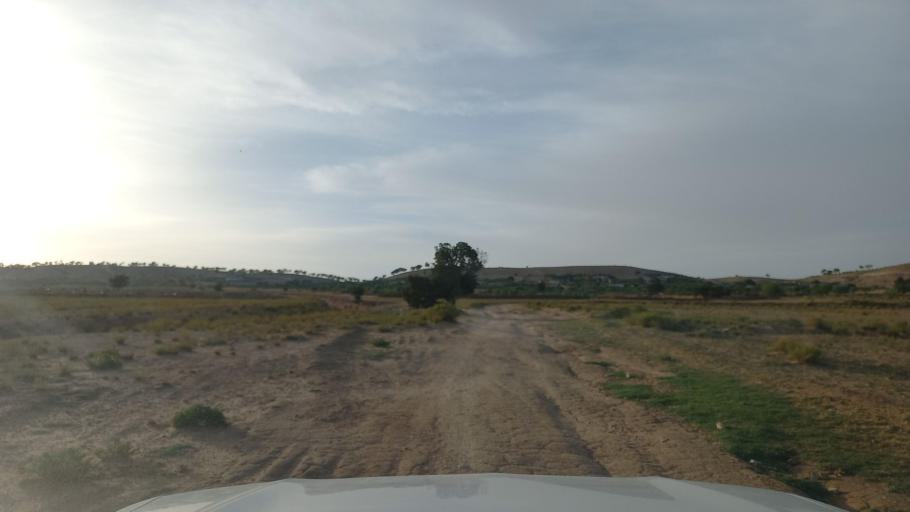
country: TN
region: Al Qasrayn
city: Sbiba
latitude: 35.4064
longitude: 8.9077
